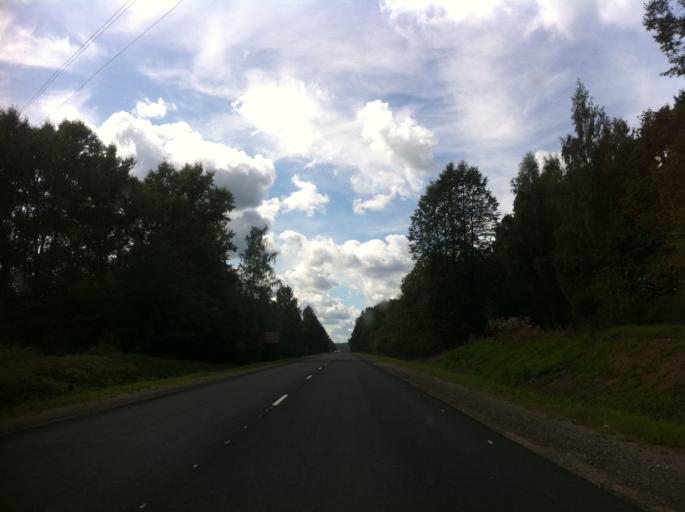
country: RU
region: Pskov
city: Izborsk
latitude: 57.7123
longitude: 27.9025
